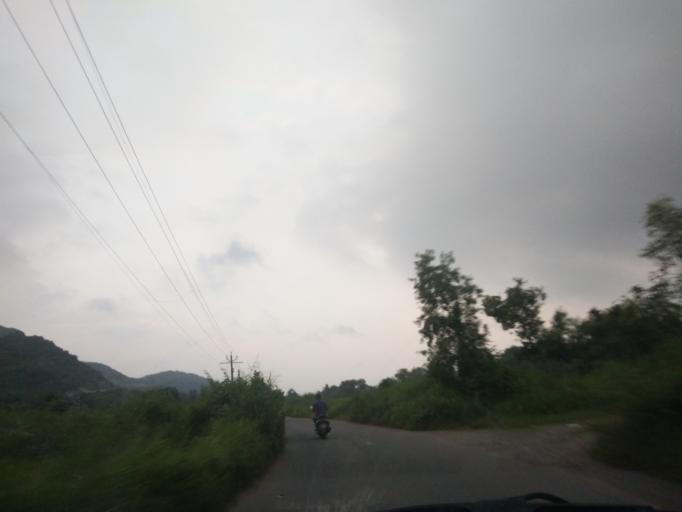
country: IN
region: Goa
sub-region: South Goa
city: Chinchinim
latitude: 15.2348
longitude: 74.0113
